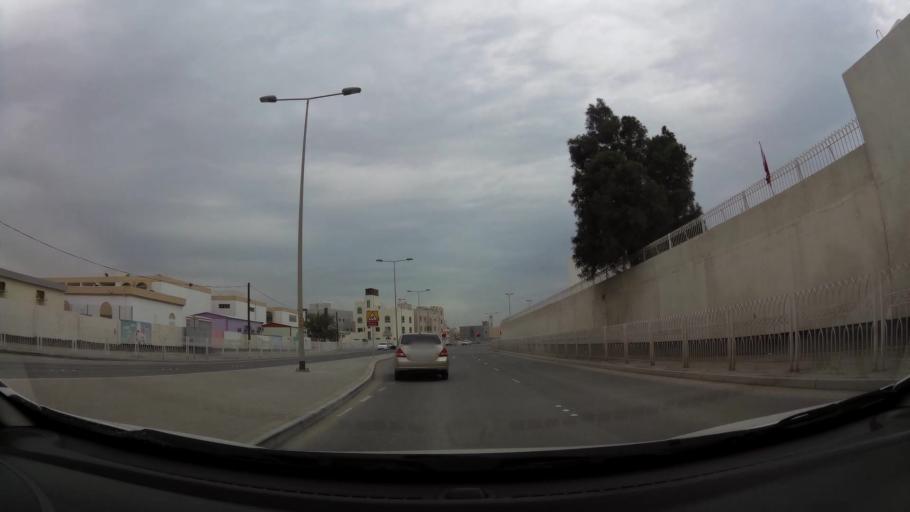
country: BH
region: Northern
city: Sitrah
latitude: 26.1555
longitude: 50.6196
